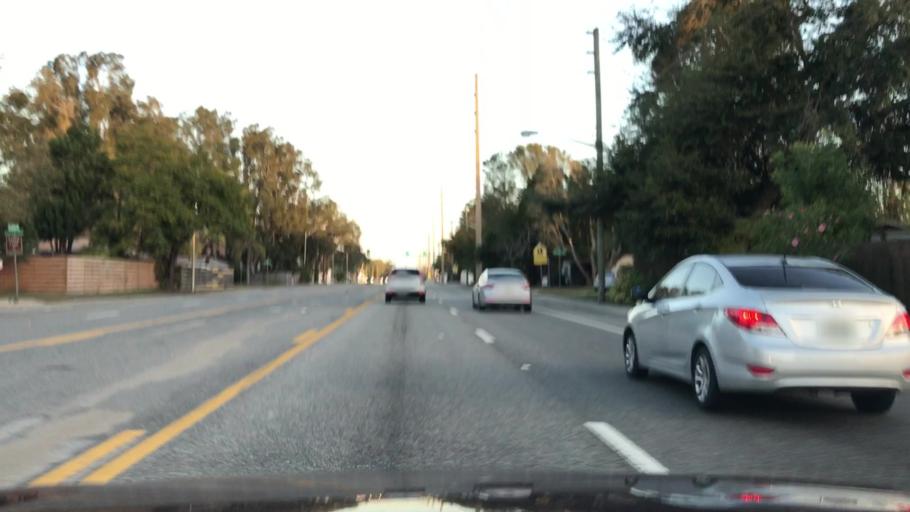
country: US
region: Florida
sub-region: Sarasota County
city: Sarasota
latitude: 27.3320
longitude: -82.5140
